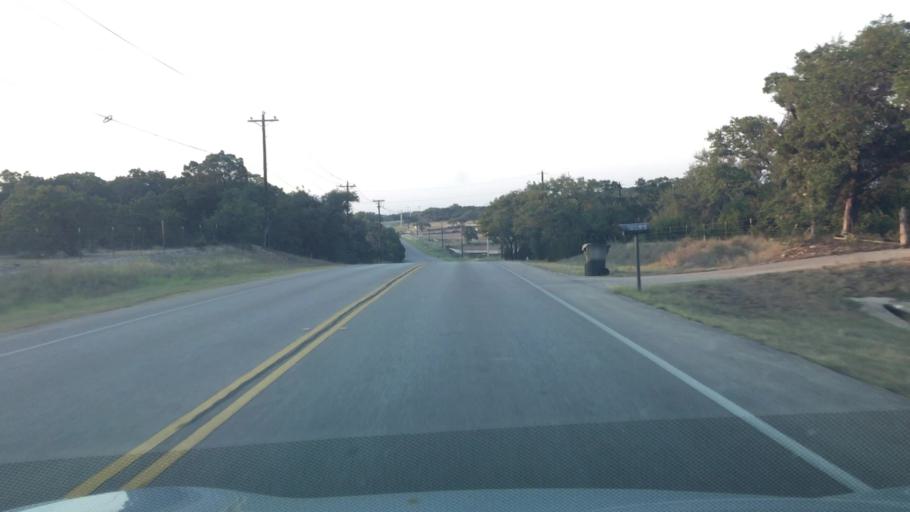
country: US
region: Texas
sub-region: Hays County
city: Dripping Springs
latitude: 30.1598
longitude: -98.0087
